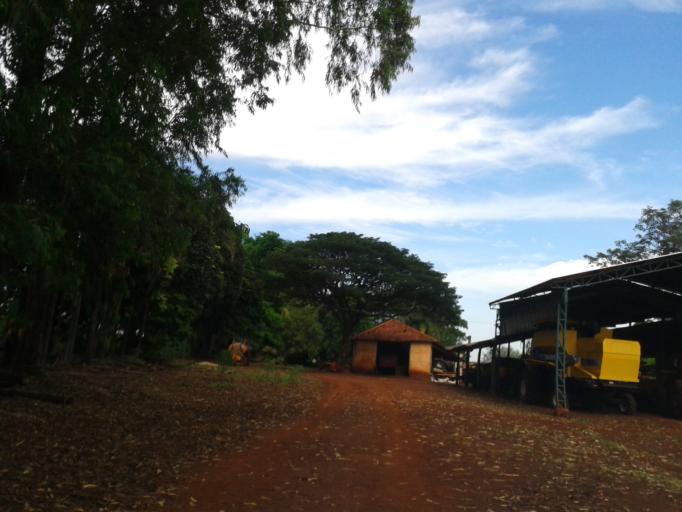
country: BR
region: Minas Gerais
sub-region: Capinopolis
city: Capinopolis
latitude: -18.6236
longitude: -49.7461
